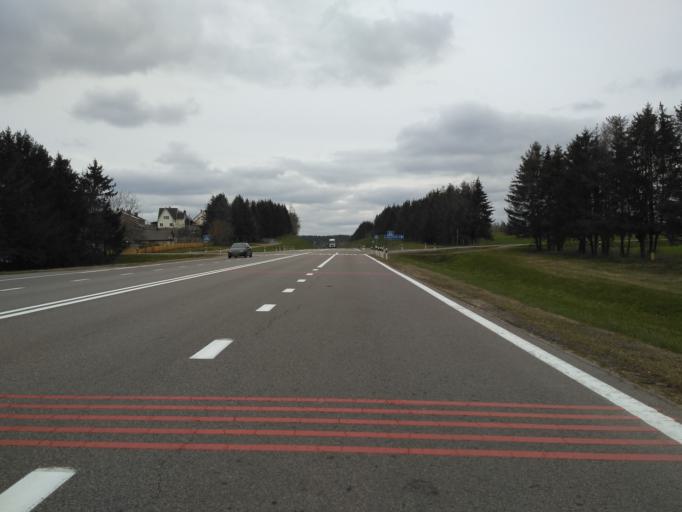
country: BY
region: Minsk
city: Slabada
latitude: 54.0300
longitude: 27.8714
